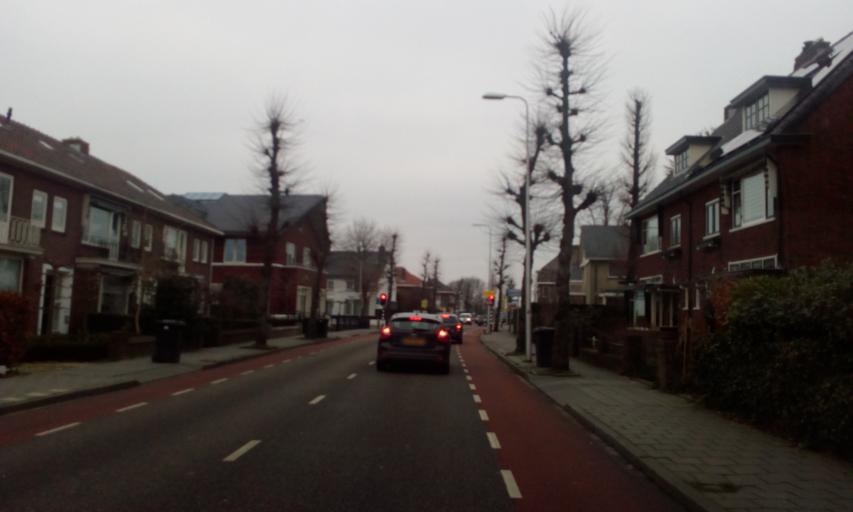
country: NL
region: South Holland
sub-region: Gemeente Waddinxveen
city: Waddinxveen
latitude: 52.0432
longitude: 4.6537
